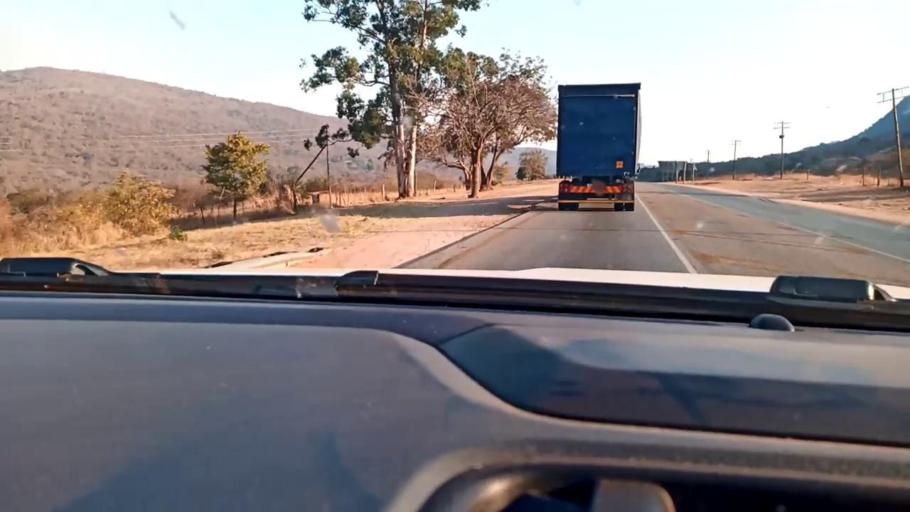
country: ZA
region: Limpopo
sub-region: Mopani District Municipality
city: Duiwelskloof
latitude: -23.6536
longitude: 30.1711
